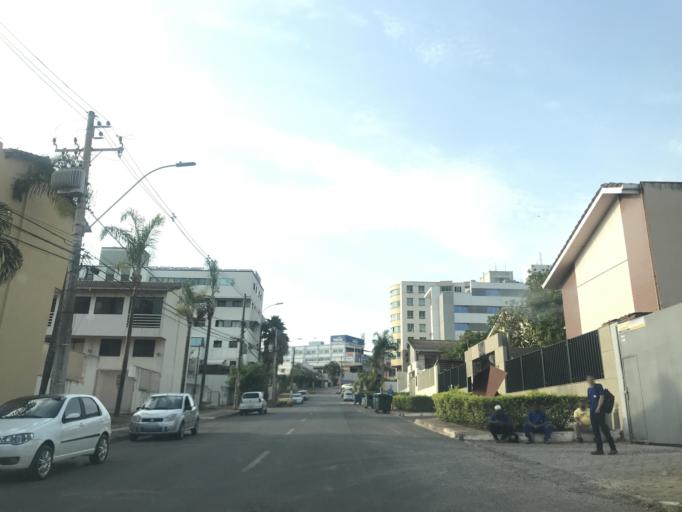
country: BR
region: Federal District
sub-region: Brasilia
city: Brasilia
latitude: -15.7147
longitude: -47.8873
